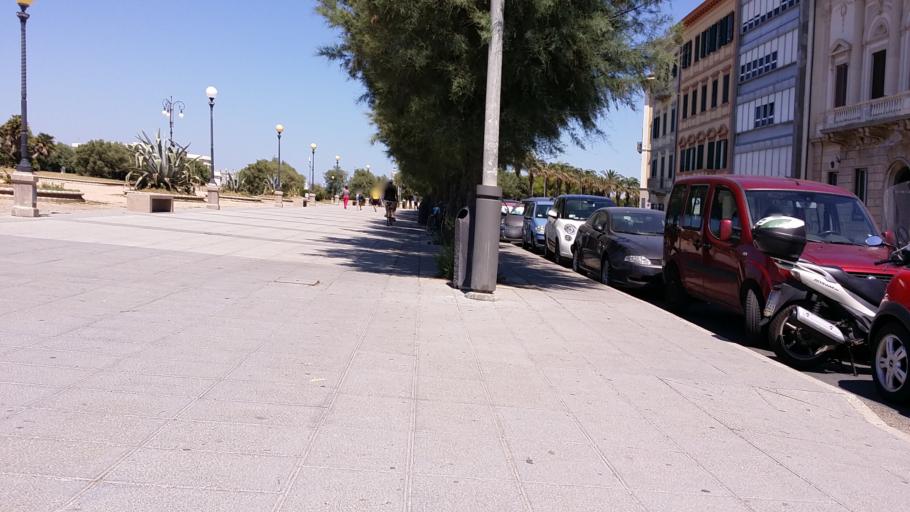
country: IT
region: Tuscany
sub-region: Provincia di Livorno
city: Livorno
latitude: 43.5335
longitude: 10.3018
